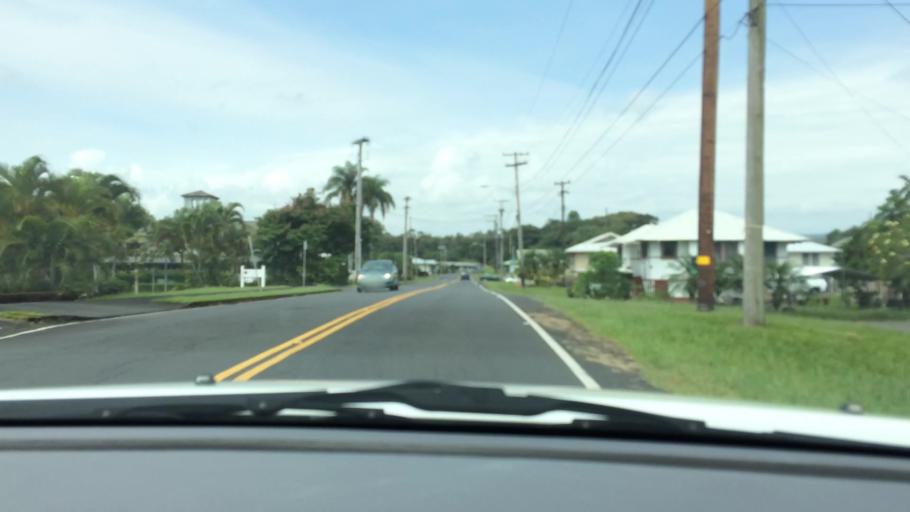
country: US
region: Hawaii
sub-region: Hawaii County
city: Hilo
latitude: 19.7118
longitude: -155.0776
